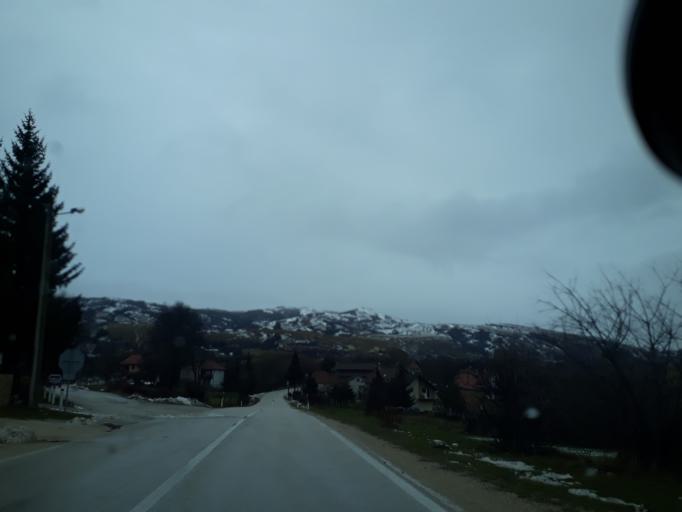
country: BA
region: Federation of Bosnia and Herzegovina
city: Tomislavgrad
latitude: 43.8378
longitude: 17.1821
